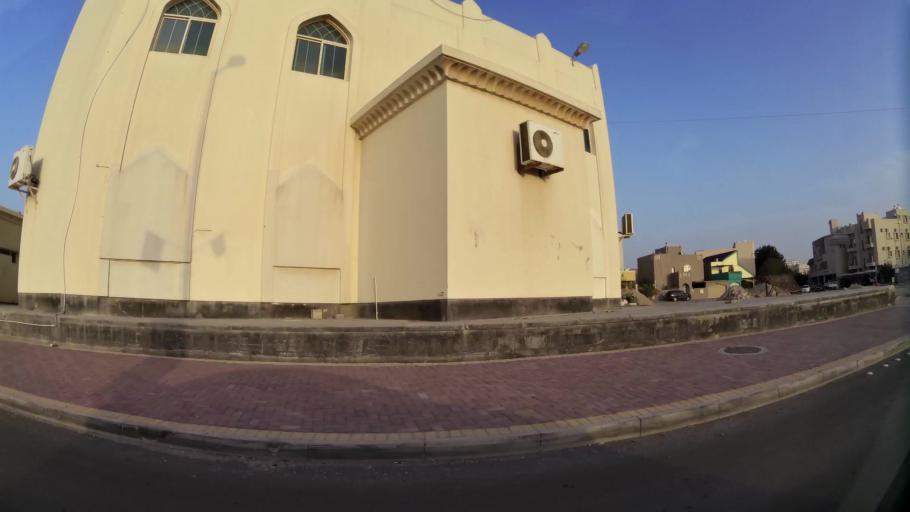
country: BH
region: Northern
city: Madinat `Isa
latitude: 26.1860
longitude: 50.4757
